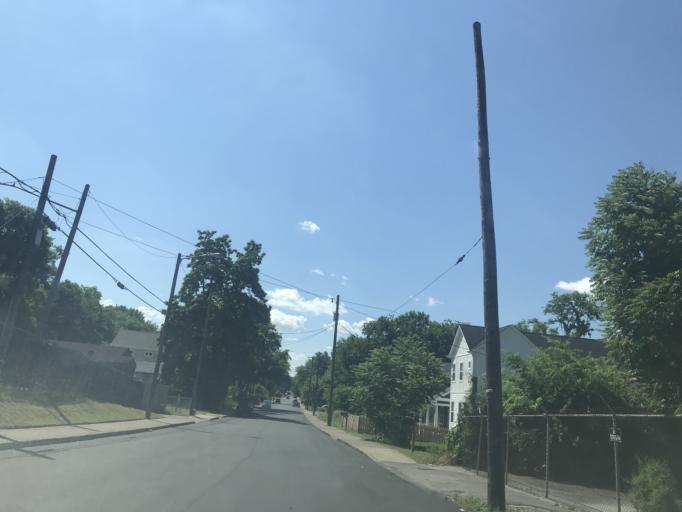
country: US
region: Tennessee
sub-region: Davidson County
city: Nashville
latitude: 36.1798
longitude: -86.8094
